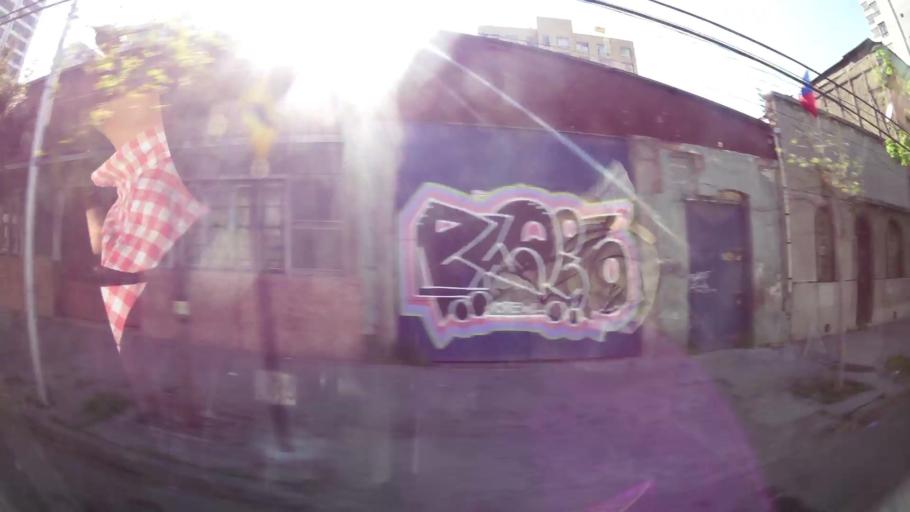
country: CL
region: Santiago Metropolitan
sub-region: Provincia de Santiago
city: Santiago
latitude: -33.4539
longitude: -70.6317
